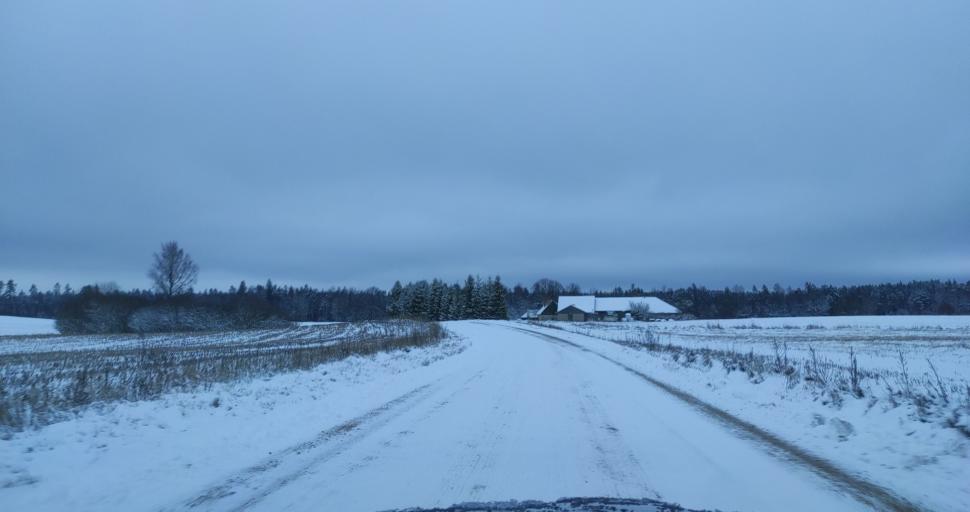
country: LV
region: Alsunga
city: Alsunga
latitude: 56.9494
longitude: 21.7518
